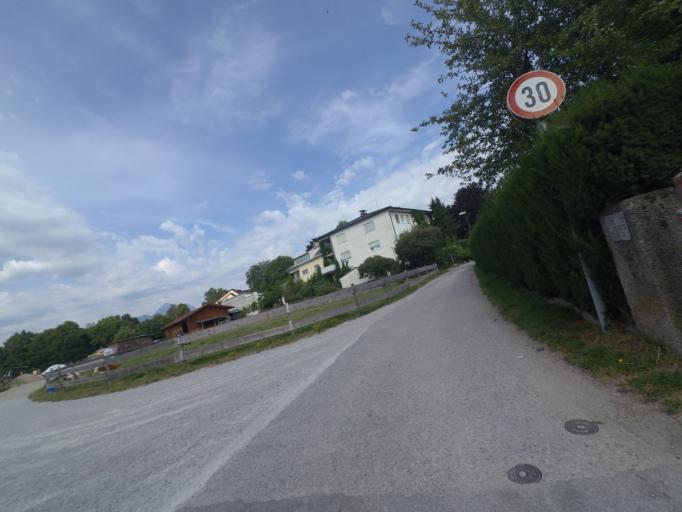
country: AT
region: Salzburg
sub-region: Salzburg Stadt
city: Salzburg
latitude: 47.7909
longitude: 13.0230
